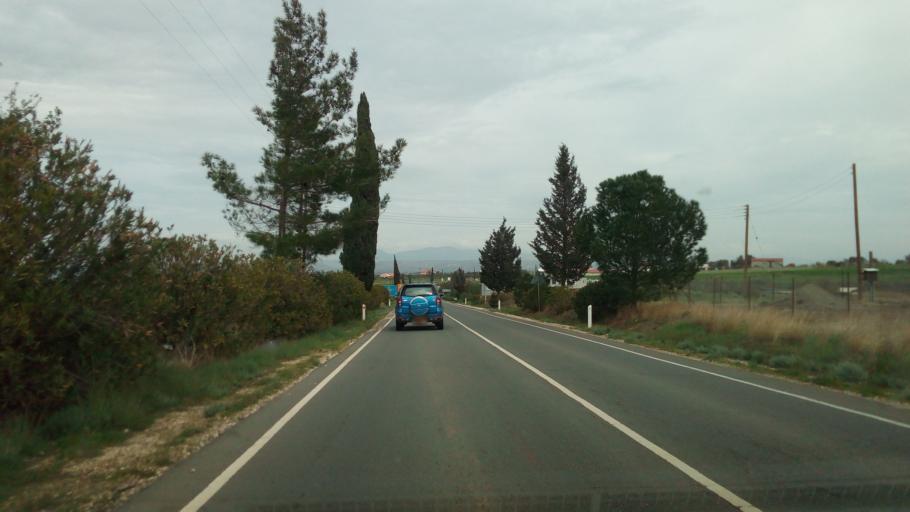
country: CY
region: Lefkosia
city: Astromeritis
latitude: 35.1281
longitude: 33.0134
